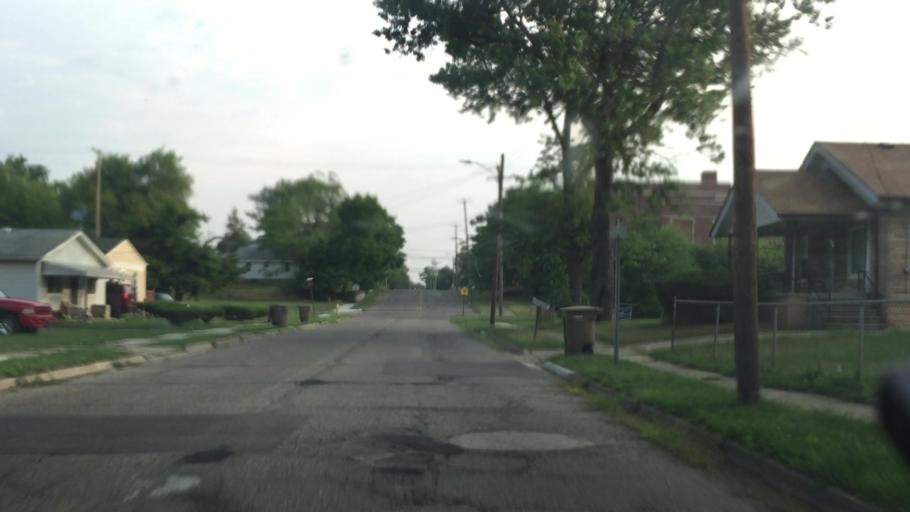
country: US
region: Michigan
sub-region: Oakland County
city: Pontiac
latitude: 42.6359
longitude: -83.2751
